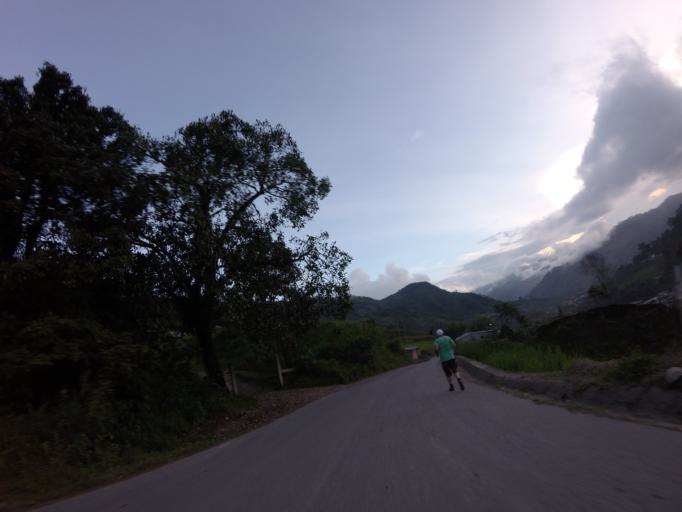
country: CO
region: Caldas
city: Manzanares
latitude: 5.2627
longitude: -75.1451
